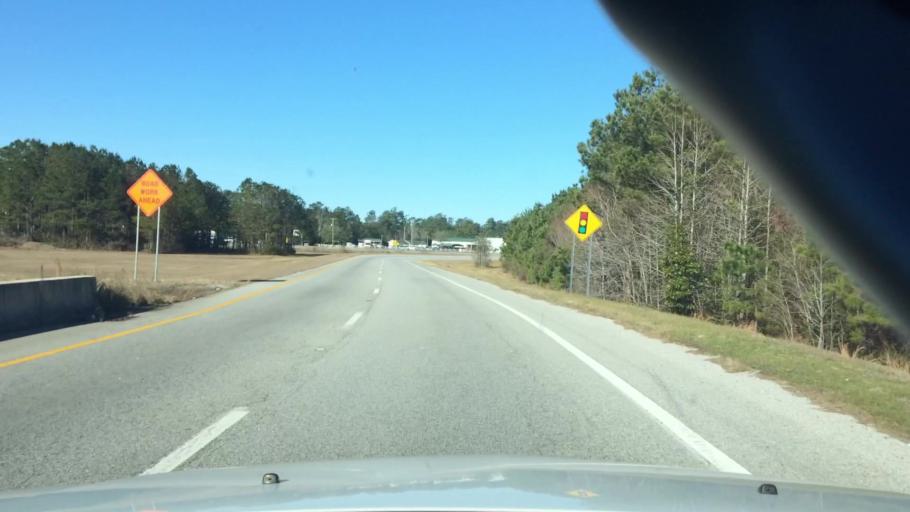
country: US
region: South Carolina
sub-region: Horry County
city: North Myrtle Beach
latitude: 33.8785
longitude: -78.6834
